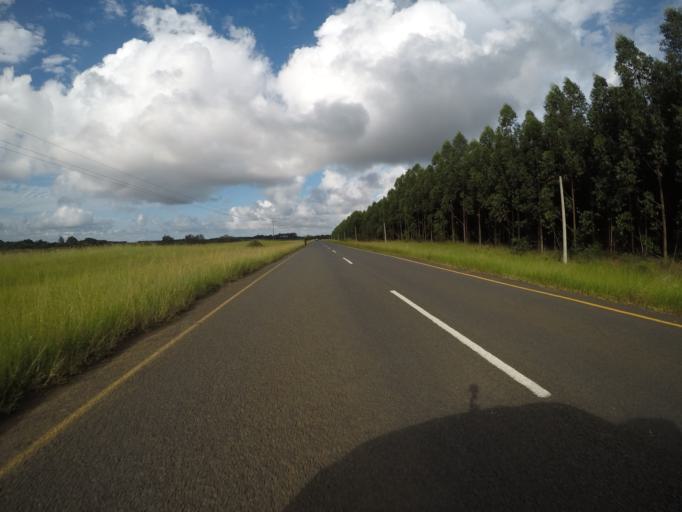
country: ZA
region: KwaZulu-Natal
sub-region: uMkhanyakude District Municipality
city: Mtubatuba
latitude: -28.3830
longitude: 32.2416
